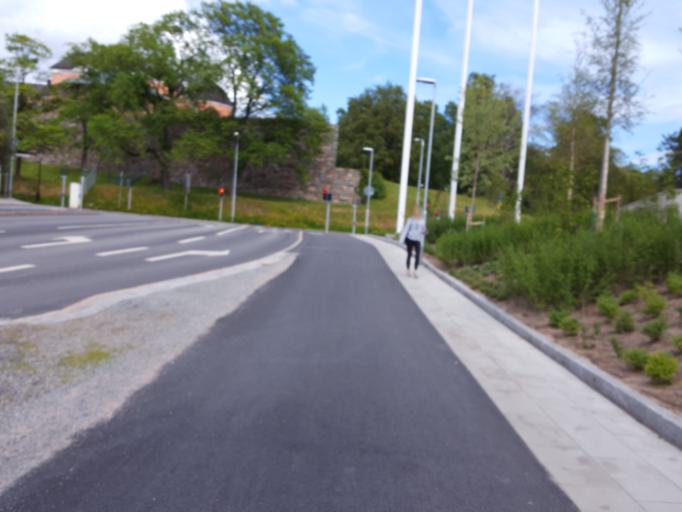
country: SE
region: Uppsala
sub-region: Uppsala Kommun
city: Uppsala
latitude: 59.8522
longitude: 17.6327
